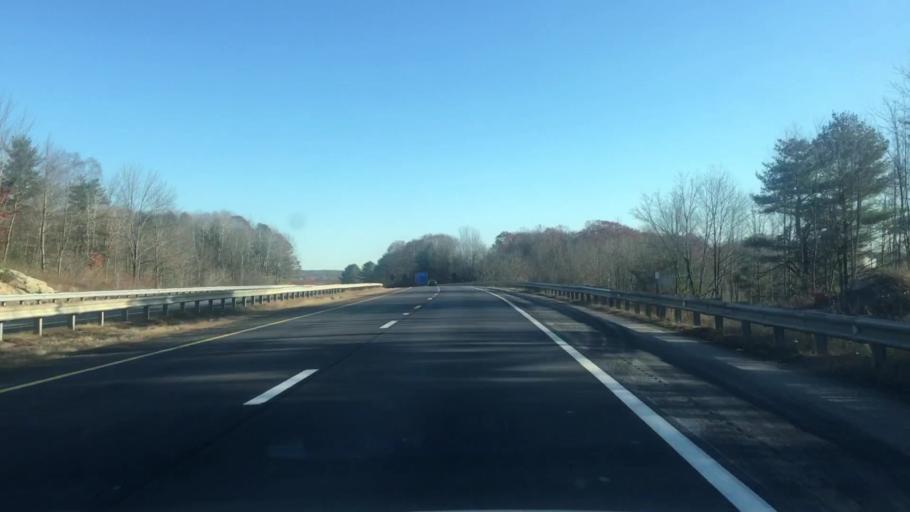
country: US
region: Maine
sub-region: Androscoggin County
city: Auburn
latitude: 44.0565
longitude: -70.2173
